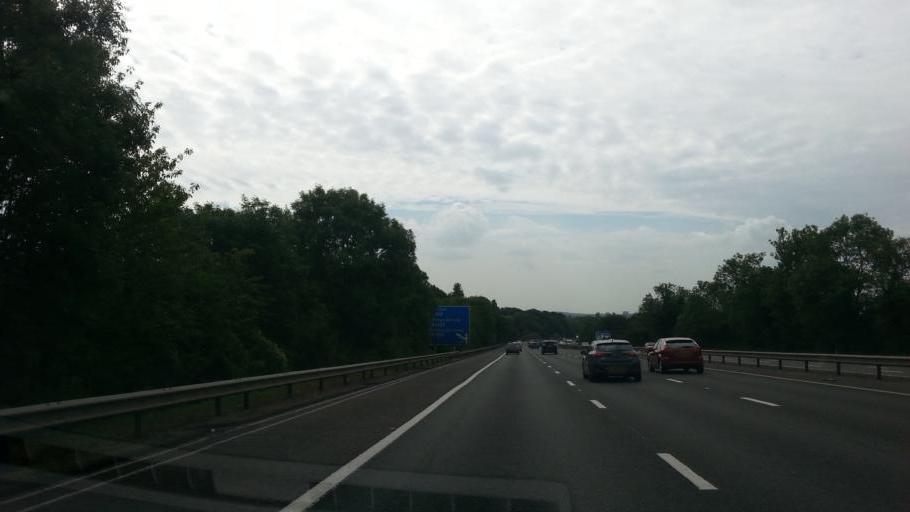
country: GB
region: England
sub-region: Hertfordshire
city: Welwyn Garden City
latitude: 51.7988
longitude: -0.2267
